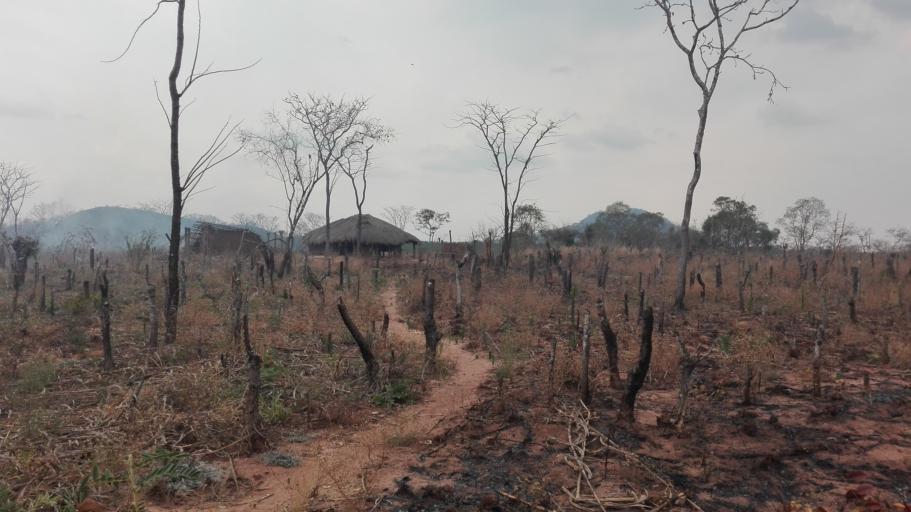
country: MZ
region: Nampula
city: Mutuali
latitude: -15.6597
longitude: 36.9262
